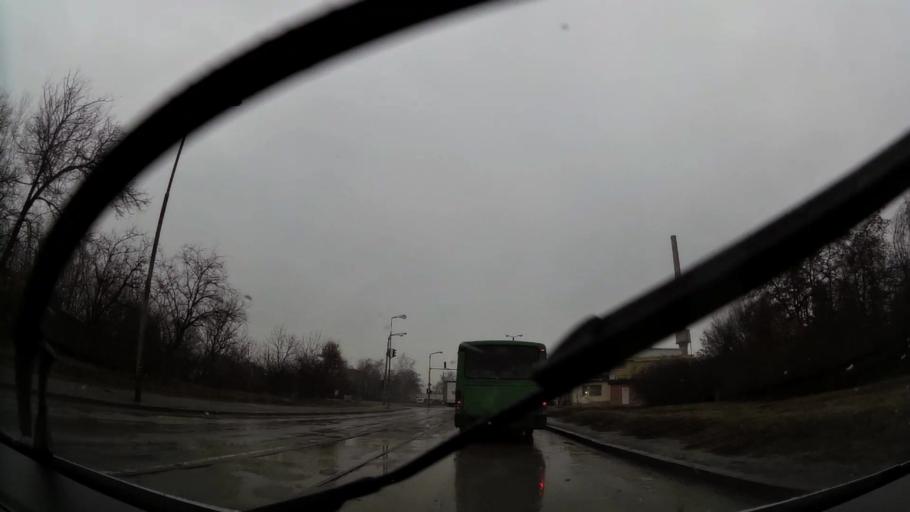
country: BG
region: Sofia-Capital
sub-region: Stolichna Obshtina
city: Sofia
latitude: 42.6630
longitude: 23.4149
